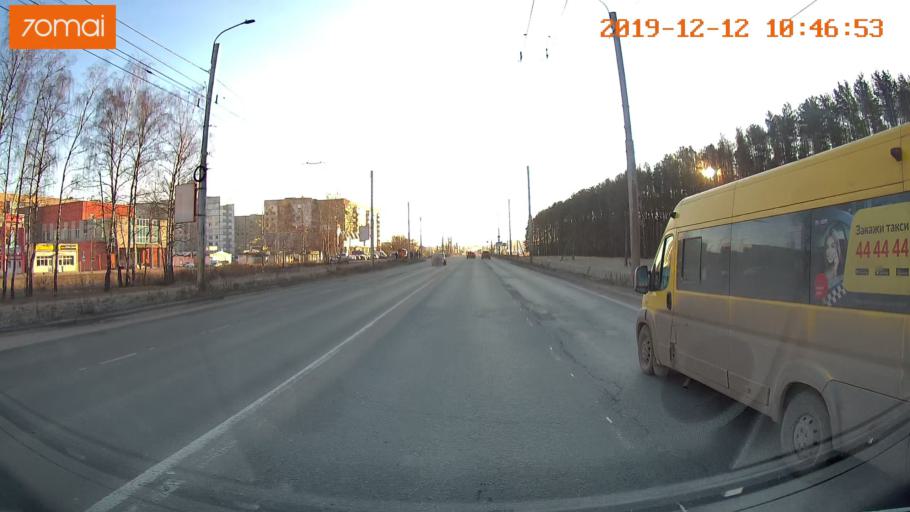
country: RU
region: Ivanovo
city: Kokhma
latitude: 56.9502
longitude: 41.0482
